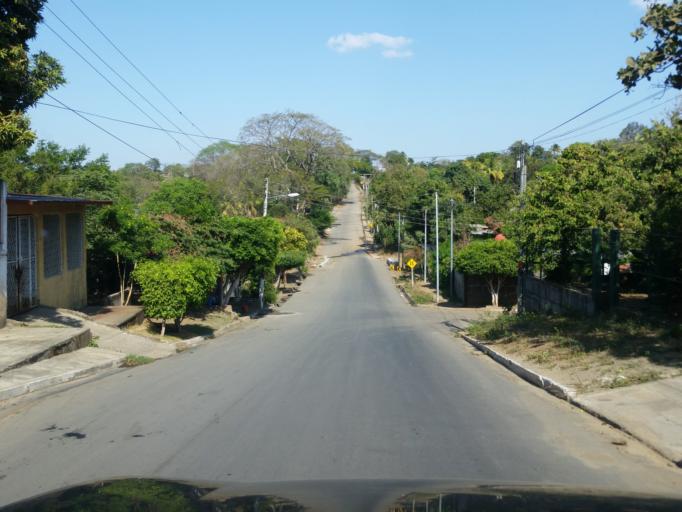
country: NI
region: Managua
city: Managua
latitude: 12.1021
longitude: -86.2955
